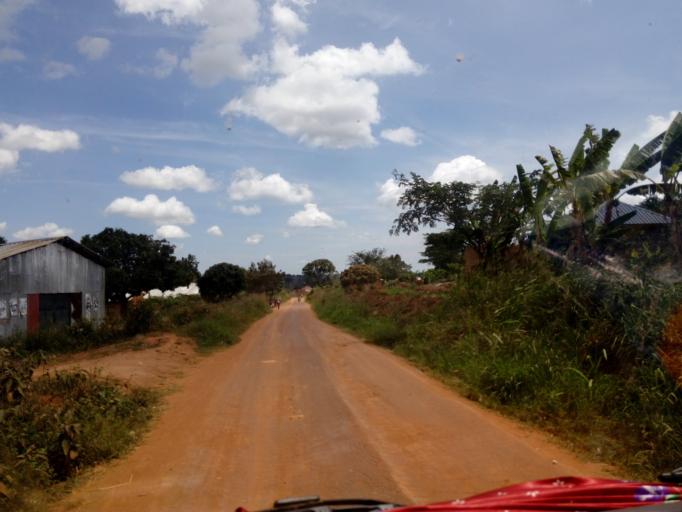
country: UG
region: Central Region
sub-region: Mubende District
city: Mubende
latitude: 0.4523
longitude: 31.6924
